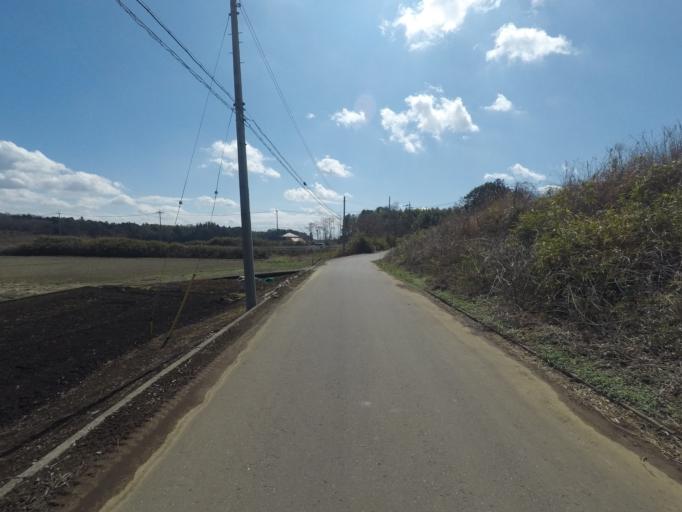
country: JP
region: Ibaraki
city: Ushiku
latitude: 36.0110
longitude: 140.0740
